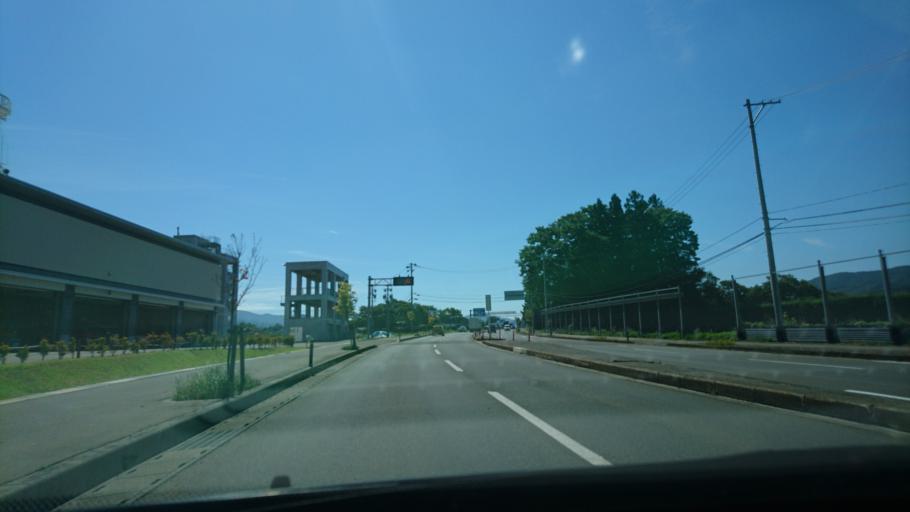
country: JP
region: Iwate
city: Tono
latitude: 39.3296
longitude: 141.5625
